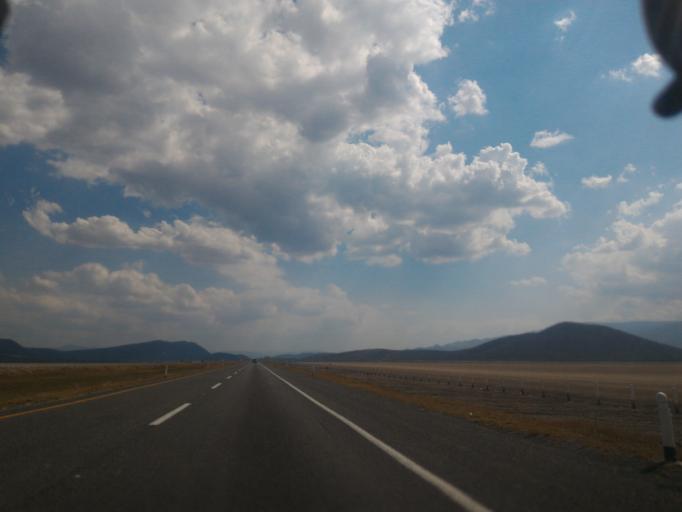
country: MX
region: Jalisco
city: Zacoalco de Torres
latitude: 20.2938
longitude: -103.5565
